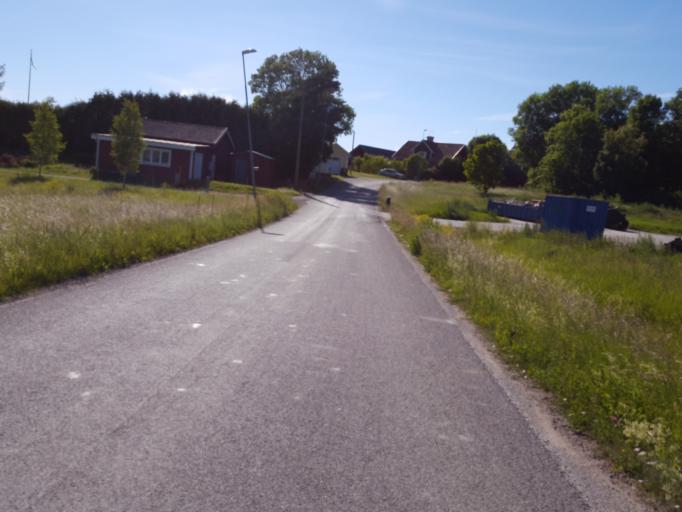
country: SE
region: Uppsala
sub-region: Uppsala Kommun
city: Saevja
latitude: 59.8314
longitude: 17.7476
